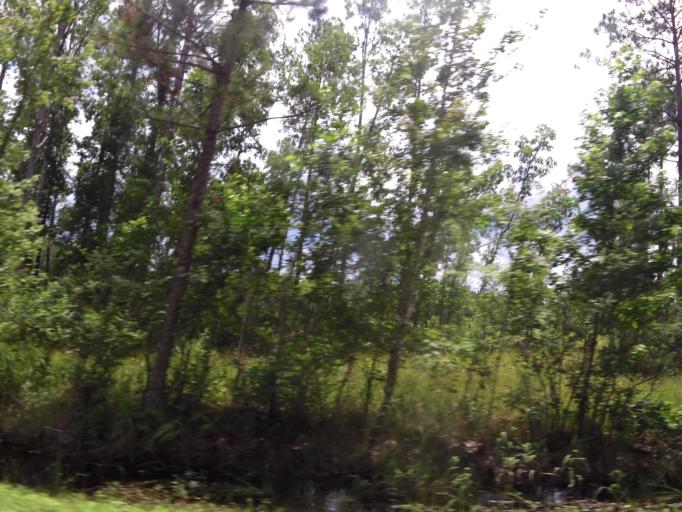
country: US
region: Florida
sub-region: Flagler County
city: Palm Coast
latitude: 29.6552
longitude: -81.3382
